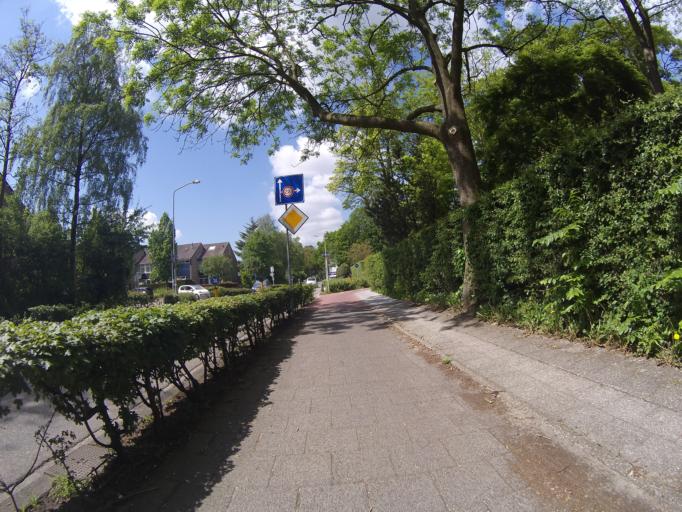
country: NL
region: North Holland
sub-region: Gemeente Laren
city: Laren
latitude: 52.2549
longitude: 5.2416
